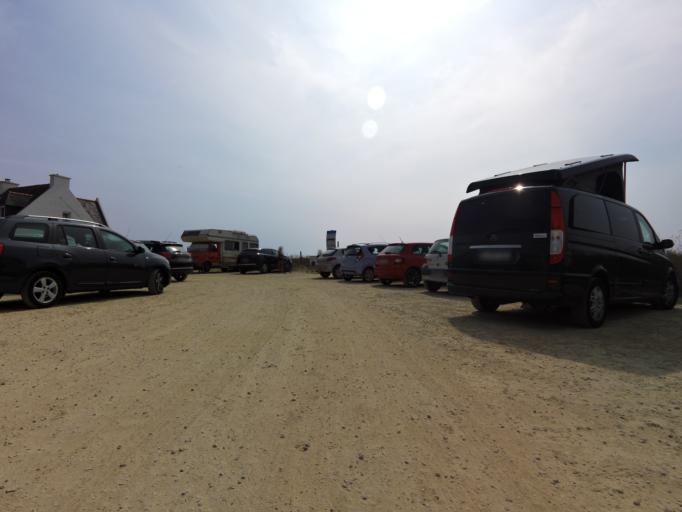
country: FR
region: Brittany
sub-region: Departement du Finistere
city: Esquibien
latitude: 48.0143
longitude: -4.5929
